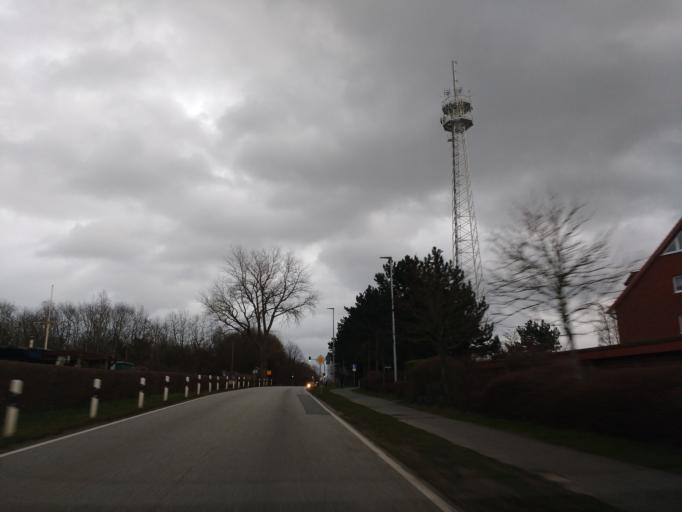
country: DE
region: Schleswig-Holstein
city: Heiligenhafen
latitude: 54.3667
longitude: 10.9966
